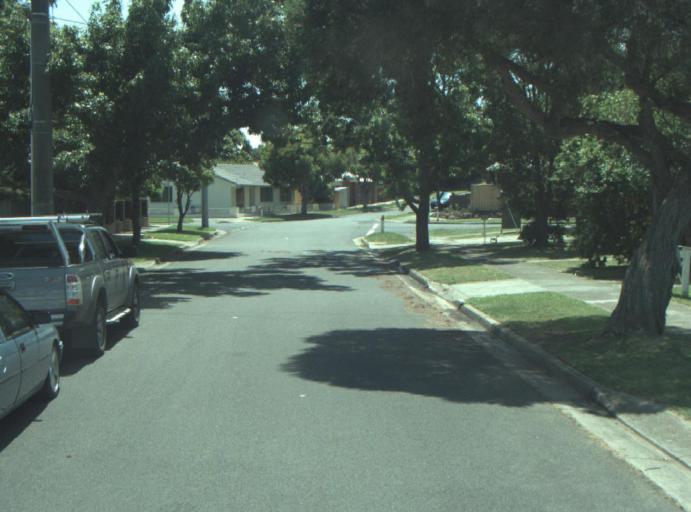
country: AU
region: Victoria
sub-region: Greater Geelong
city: Wandana Heights
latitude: -38.1586
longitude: 144.3242
